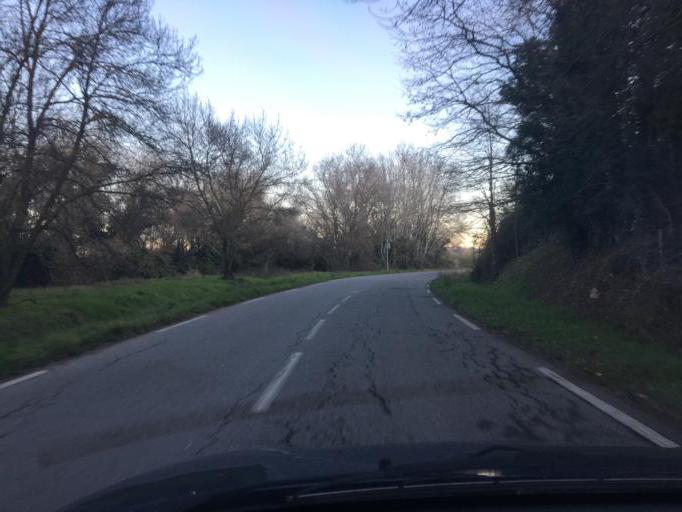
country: FR
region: Provence-Alpes-Cote d'Azur
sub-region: Departement des Bouches-du-Rhone
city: Mallemort
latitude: 43.7336
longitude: 5.1824
